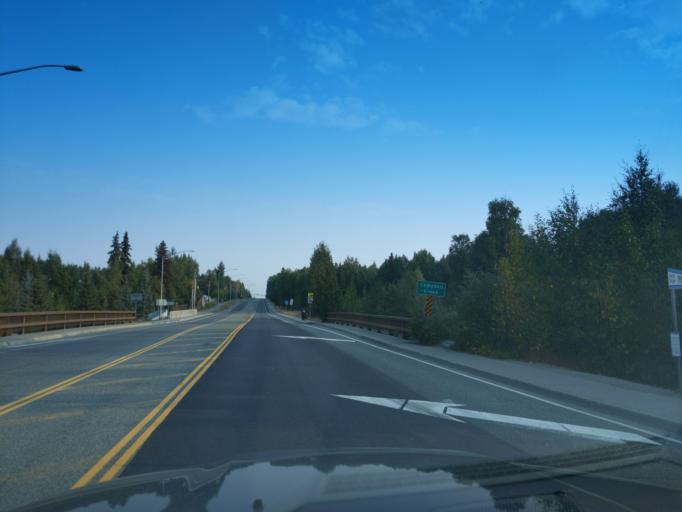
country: US
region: Alaska
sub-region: Anchorage Municipality
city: Anchorage
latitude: 61.1455
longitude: -149.8921
